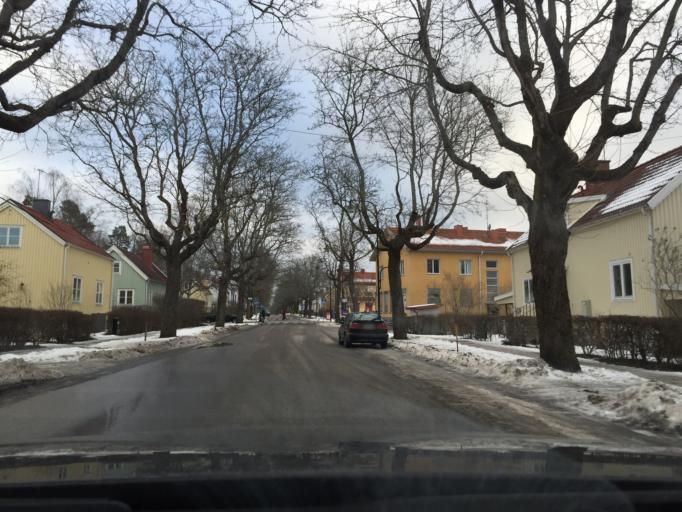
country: SE
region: Stockholm
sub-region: Stockholms Kommun
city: Bromma
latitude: 59.3477
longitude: 17.9069
